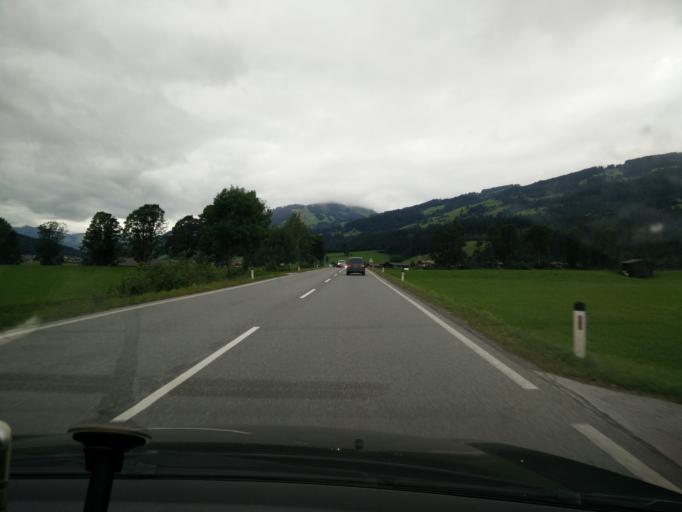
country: AT
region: Tyrol
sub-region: Politischer Bezirk Kitzbuhel
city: Kirchberg in Tirol
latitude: 47.4517
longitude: 12.2973
